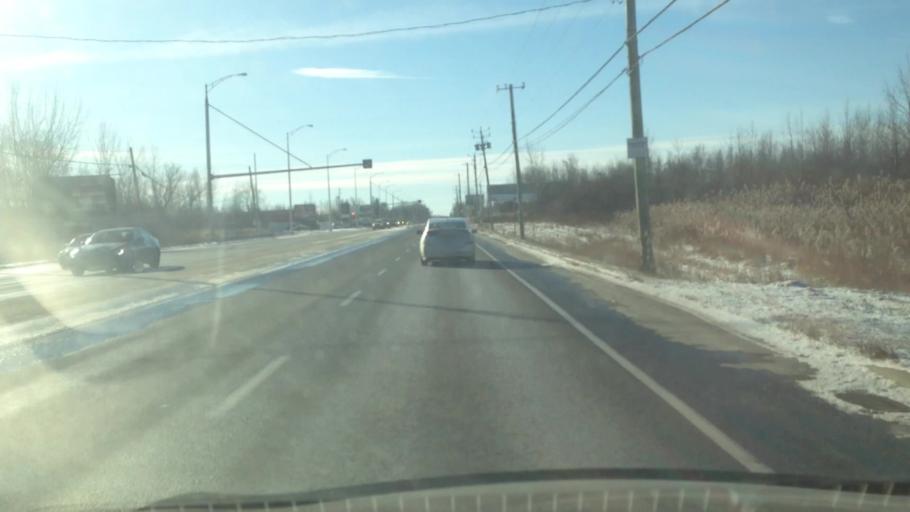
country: CA
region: Quebec
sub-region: Monteregie
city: Chateauguay
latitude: 45.3907
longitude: -73.6973
